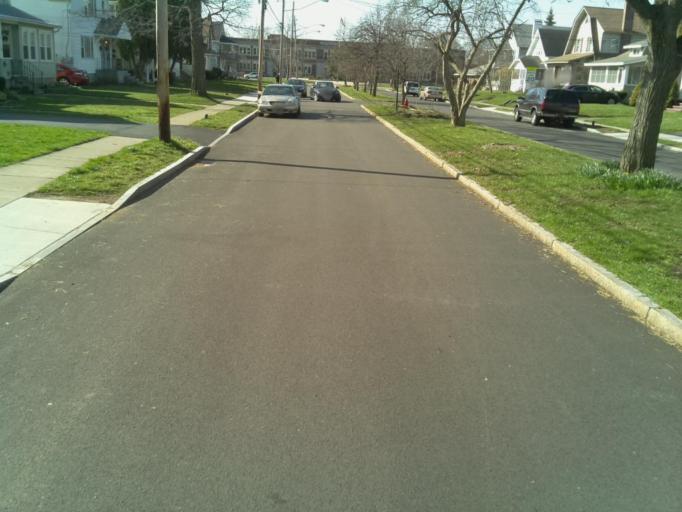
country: US
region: New York
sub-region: Onondaga County
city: Lyncourt
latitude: 43.0613
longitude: -76.1105
